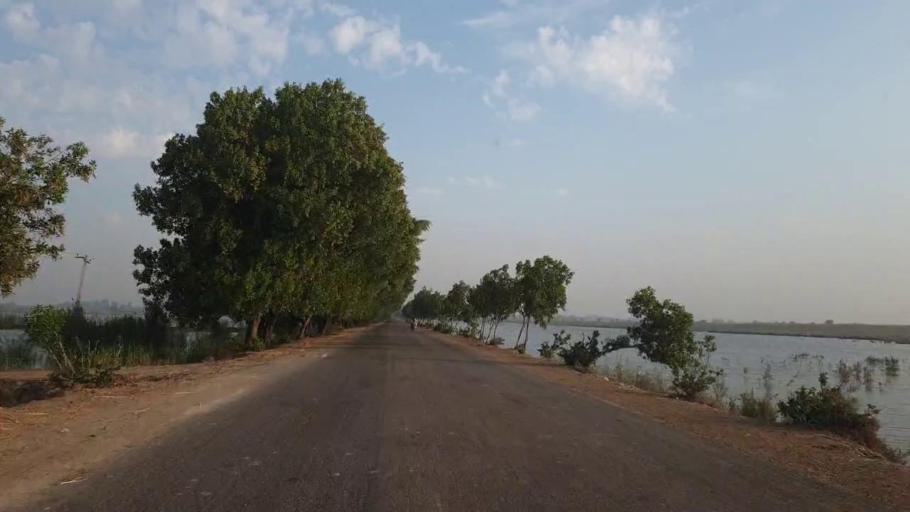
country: PK
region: Sindh
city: Tando Bago
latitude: 24.7455
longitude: 68.9484
